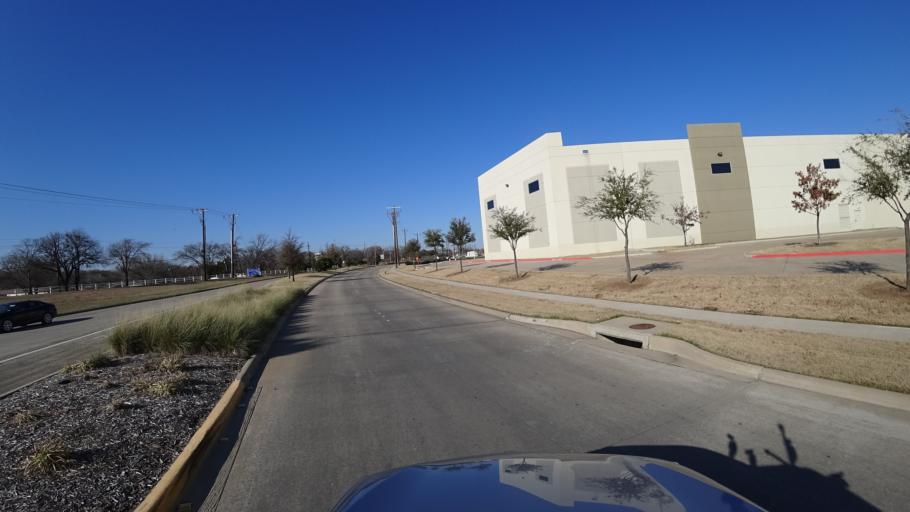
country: US
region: Texas
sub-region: Dallas County
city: Coppell
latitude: 32.9954
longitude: -97.0153
